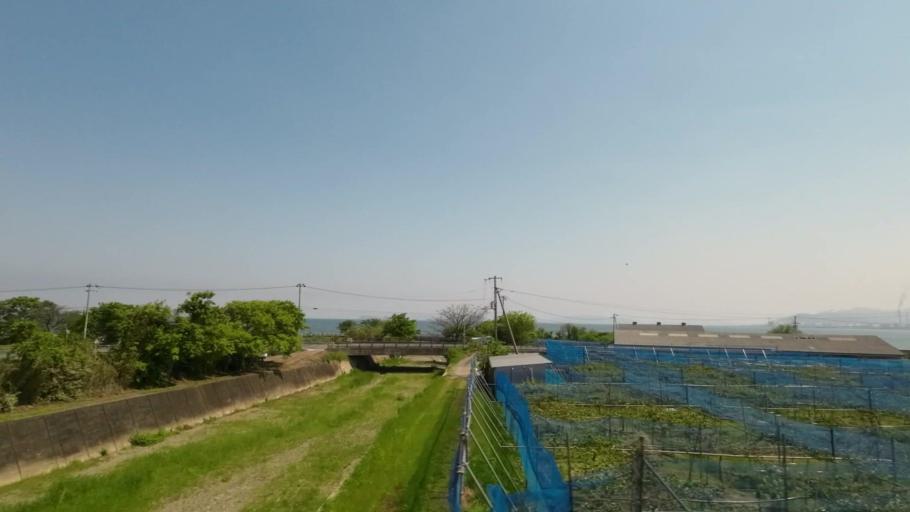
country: JP
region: Ehime
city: Kawanoecho
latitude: 33.9698
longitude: 133.4849
